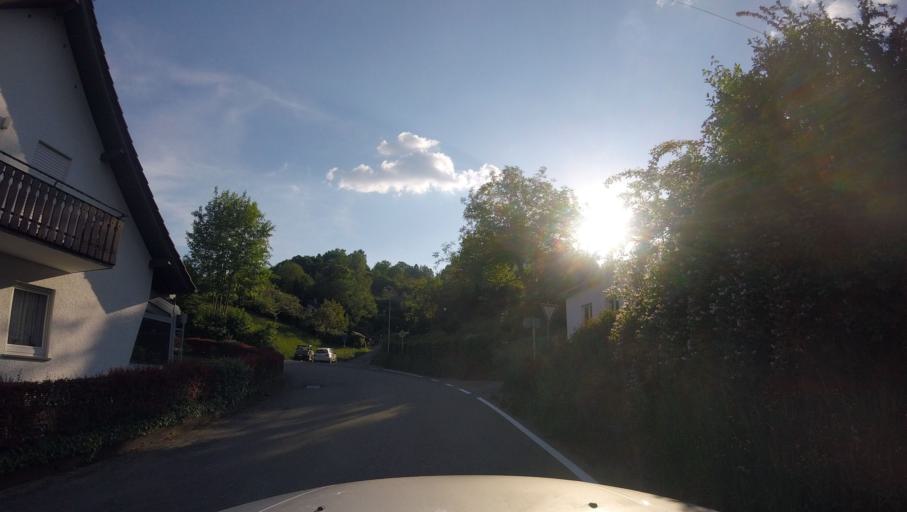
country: DE
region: Baden-Wuerttemberg
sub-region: Regierungsbezirk Stuttgart
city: Spiegelberg
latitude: 49.0381
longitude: 9.4447
